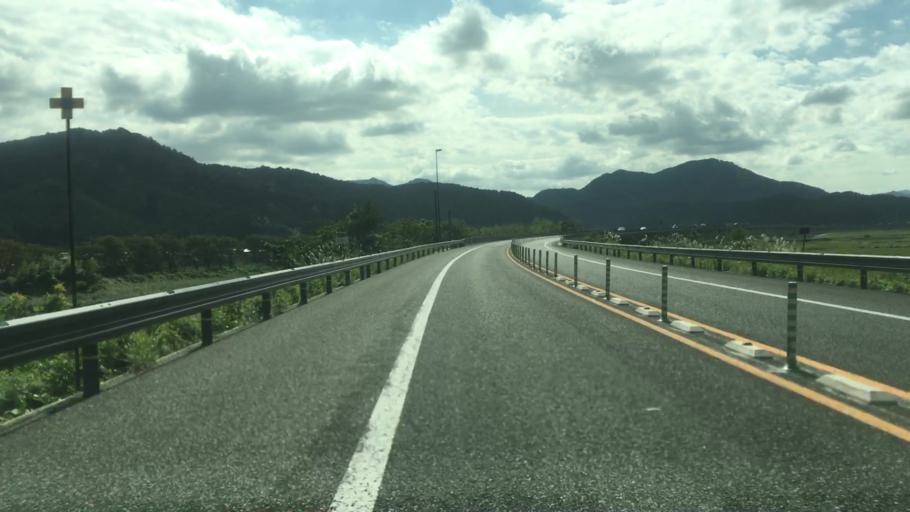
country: JP
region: Kyoto
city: Fukuchiyama
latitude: 35.2048
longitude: 135.0407
